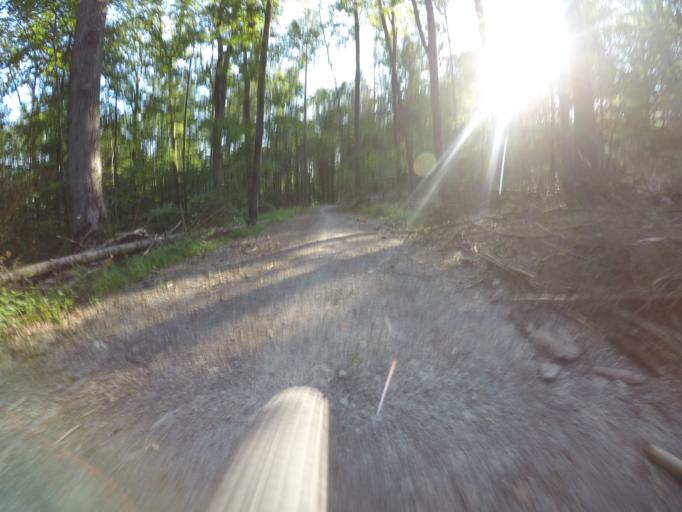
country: DE
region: Baden-Wuerttemberg
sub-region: Regierungsbezirk Stuttgart
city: Gerlingen
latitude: 48.7525
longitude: 9.0939
